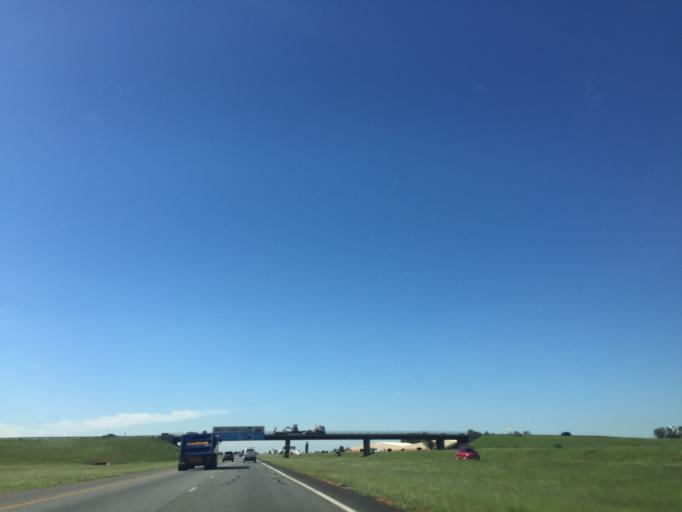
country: ZA
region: Gauteng
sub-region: Sedibeng District Municipality
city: Meyerton
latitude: -26.4154
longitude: 28.0778
